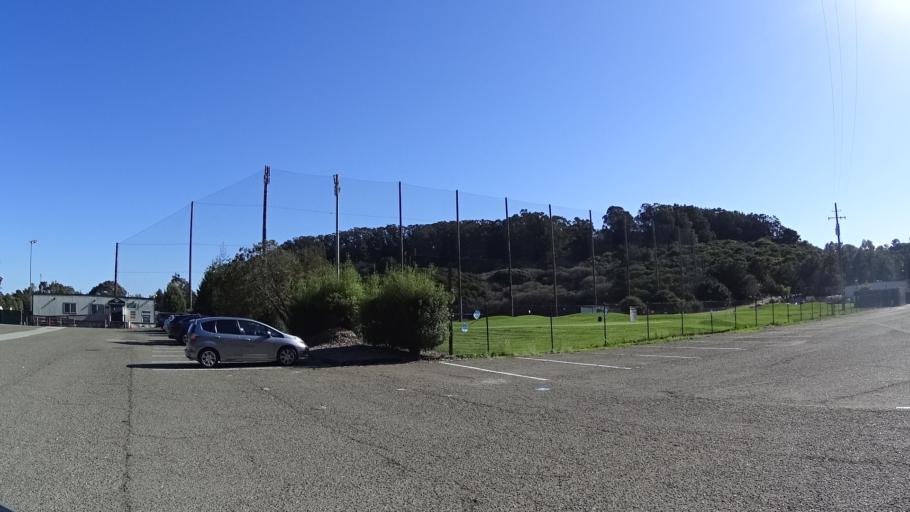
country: US
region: California
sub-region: San Mateo County
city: San Bruno
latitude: 37.6293
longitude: -122.4365
